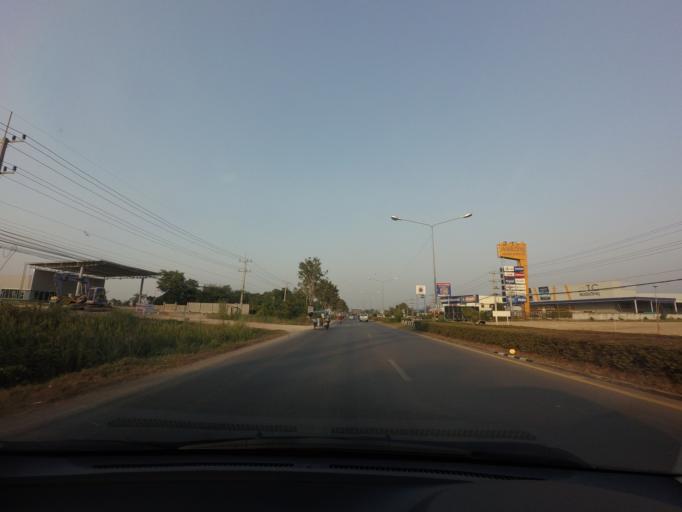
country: TH
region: Sukhothai
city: Sukhothai
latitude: 17.0179
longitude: 99.8113
